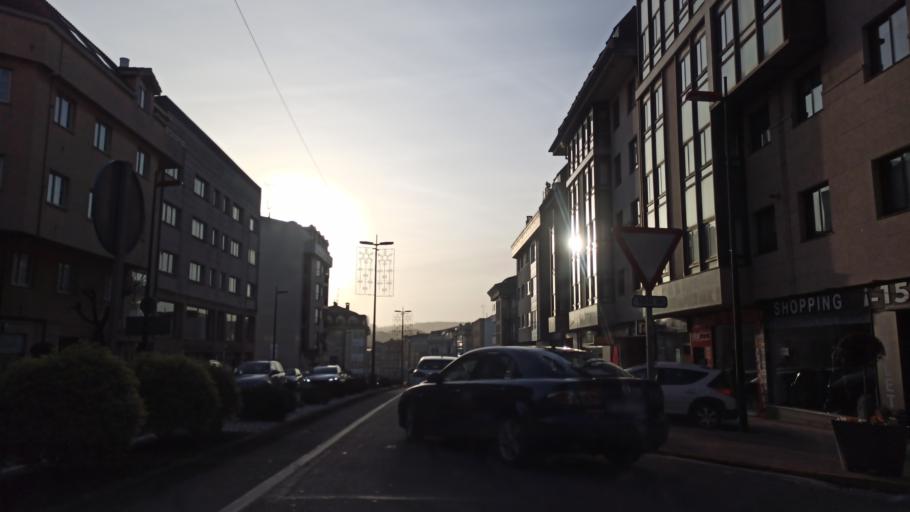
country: ES
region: Galicia
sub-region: Provincia da Coruna
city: Cambre
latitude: 43.3193
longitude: -8.3542
